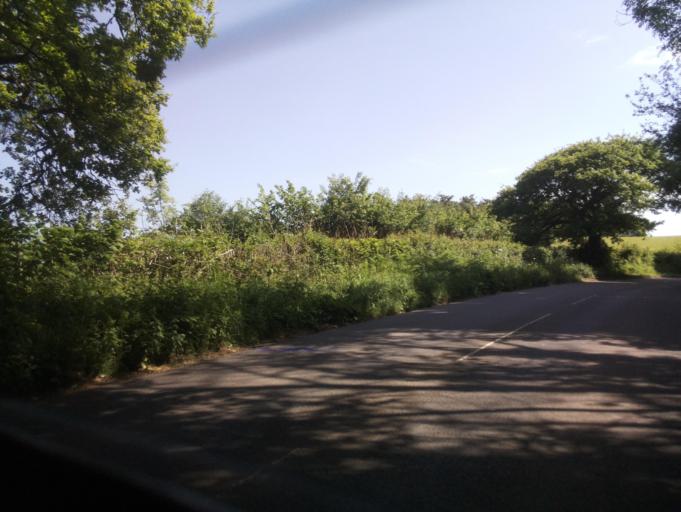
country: GB
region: England
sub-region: Devon
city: Marldon
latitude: 50.4451
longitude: -3.6151
